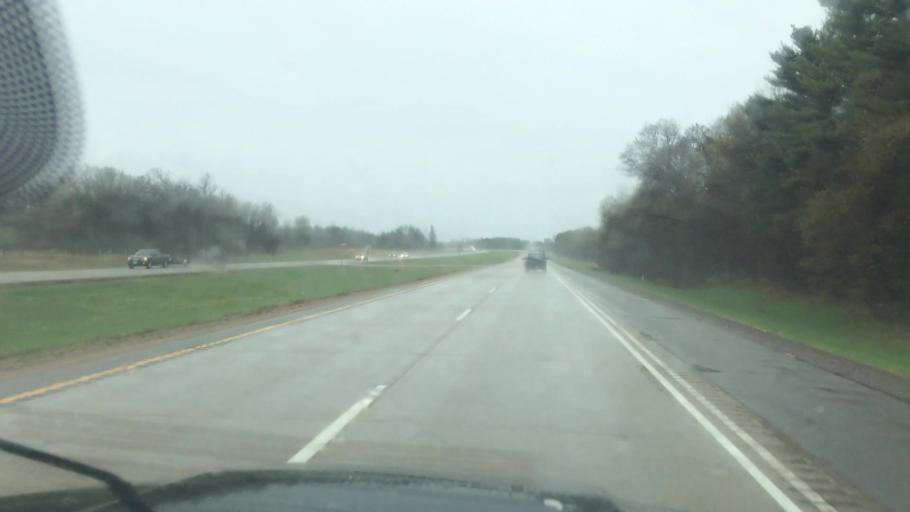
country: US
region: Wisconsin
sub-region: Portage County
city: Stevens Point
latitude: 44.6406
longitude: -89.6358
